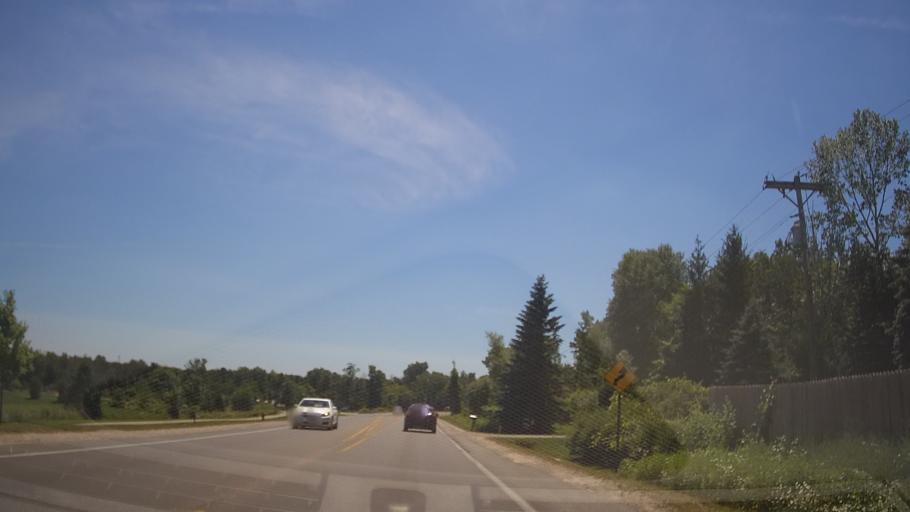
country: US
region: Michigan
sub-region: Grand Traverse County
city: Traverse City
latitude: 44.7373
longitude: -85.6559
